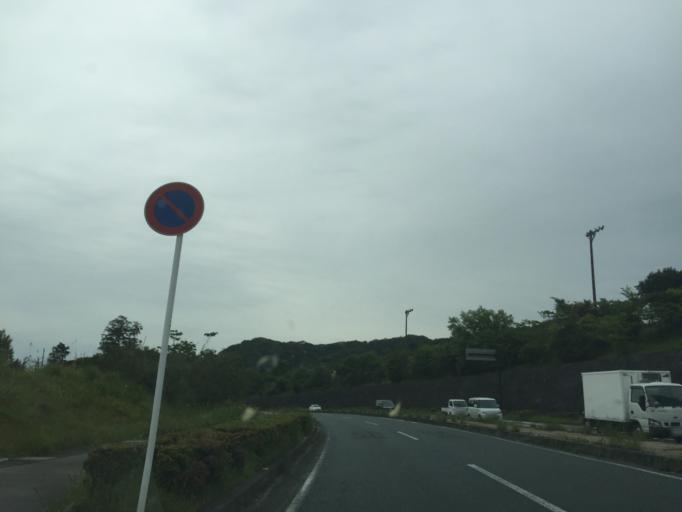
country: JP
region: Shizuoka
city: Kakegawa
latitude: 34.7515
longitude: 137.9751
